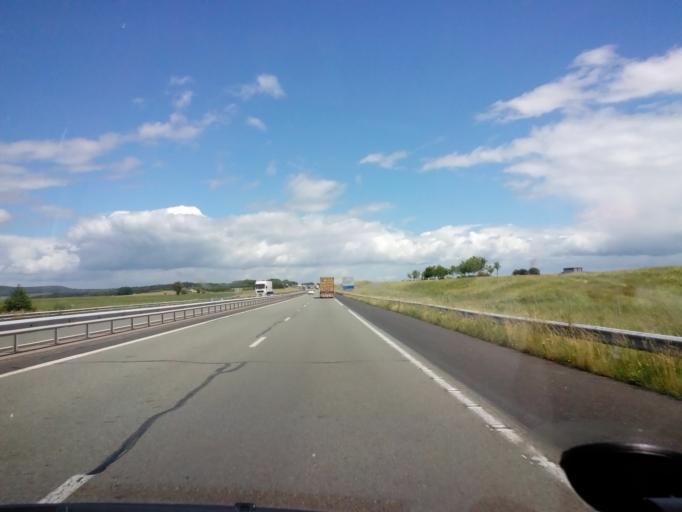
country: FR
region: Lorraine
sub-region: Departement des Vosges
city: Lamarche
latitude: 48.1360
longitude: 5.6763
